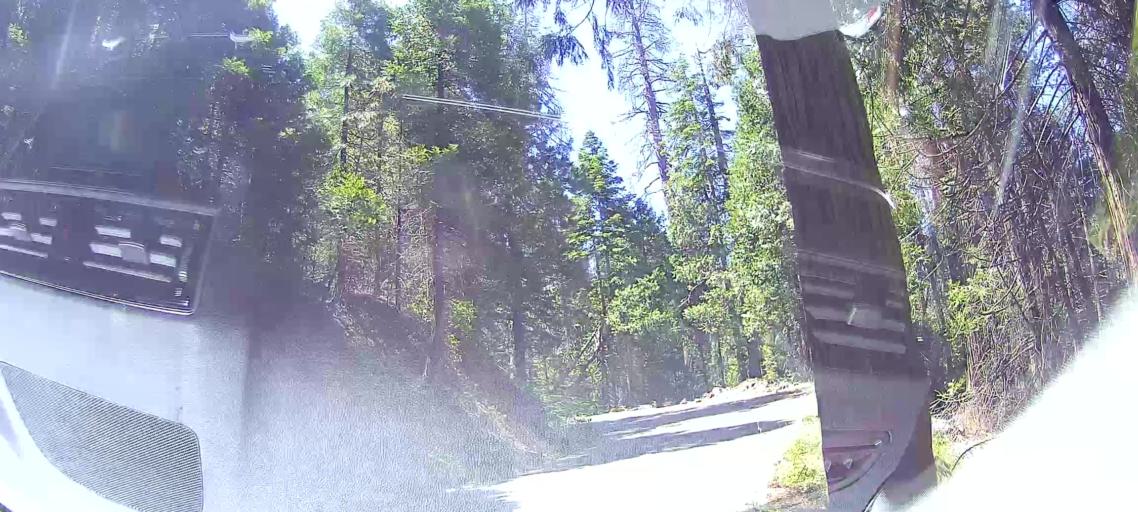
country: US
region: California
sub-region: Tulare County
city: Three Rivers
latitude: 36.5613
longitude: -118.7848
